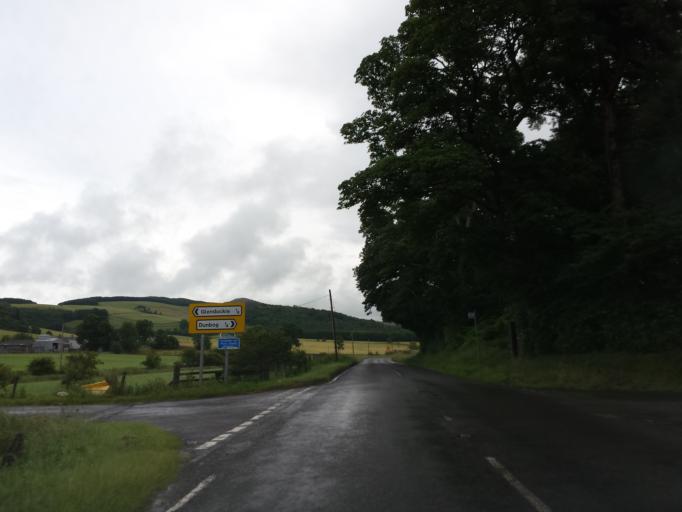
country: GB
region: Scotland
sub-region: Perth and Kinross
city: Errol
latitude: 56.3522
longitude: -3.1624
